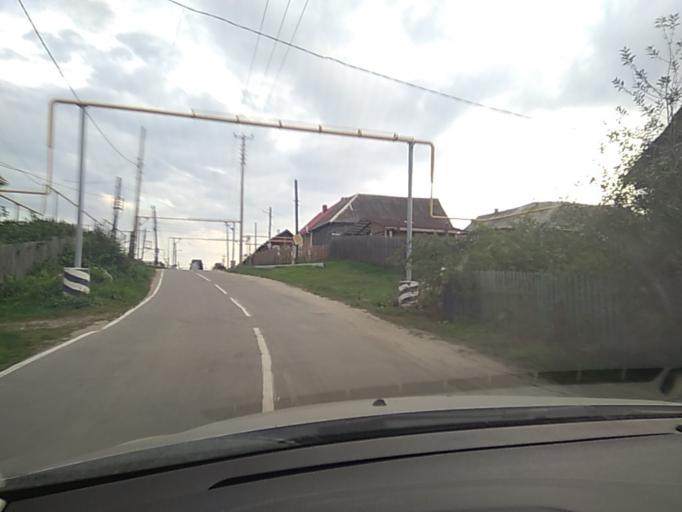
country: RU
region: Chelyabinsk
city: Kyshtym
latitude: 55.6966
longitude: 60.5321
